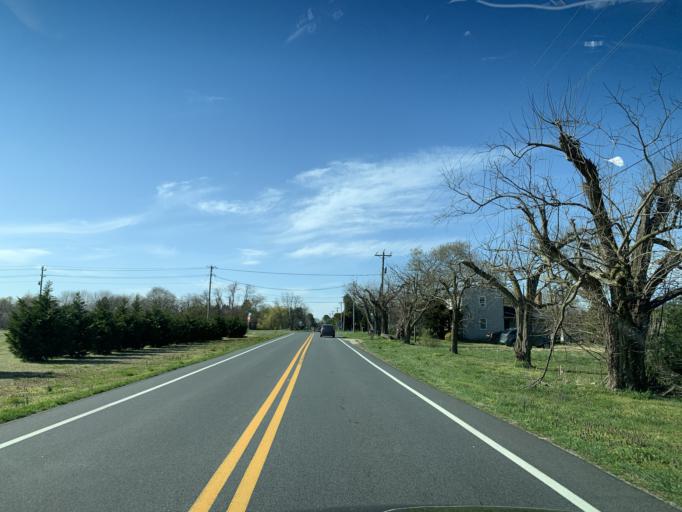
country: US
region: Delaware
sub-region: Kent County
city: Woodside East
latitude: 39.0330
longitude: -75.5474
